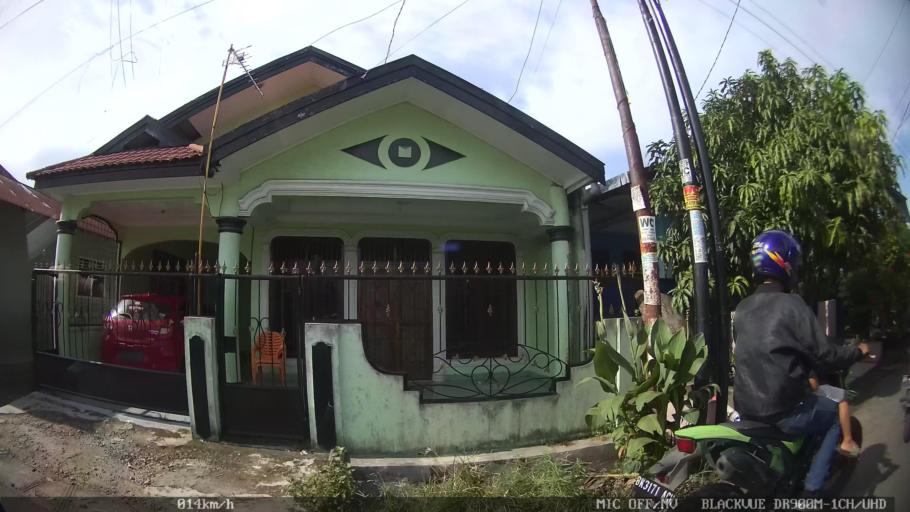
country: ID
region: North Sumatra
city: Medan
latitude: 3.6116
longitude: 98.6508
